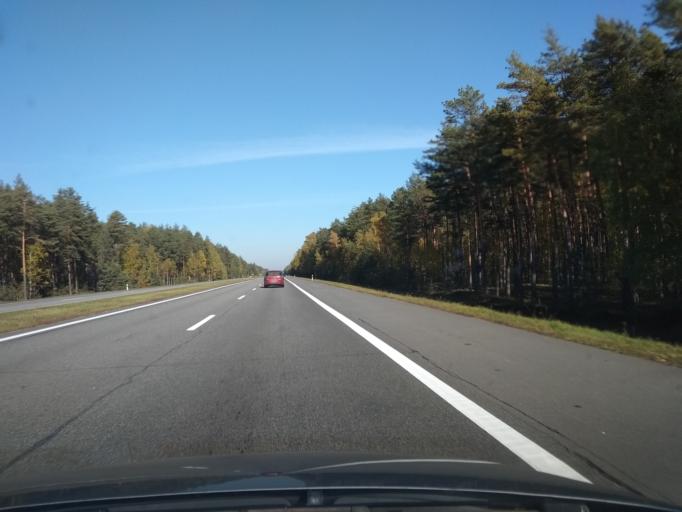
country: BY
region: Brest
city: Baranovichi
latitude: 52.9373
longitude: 25.7037
